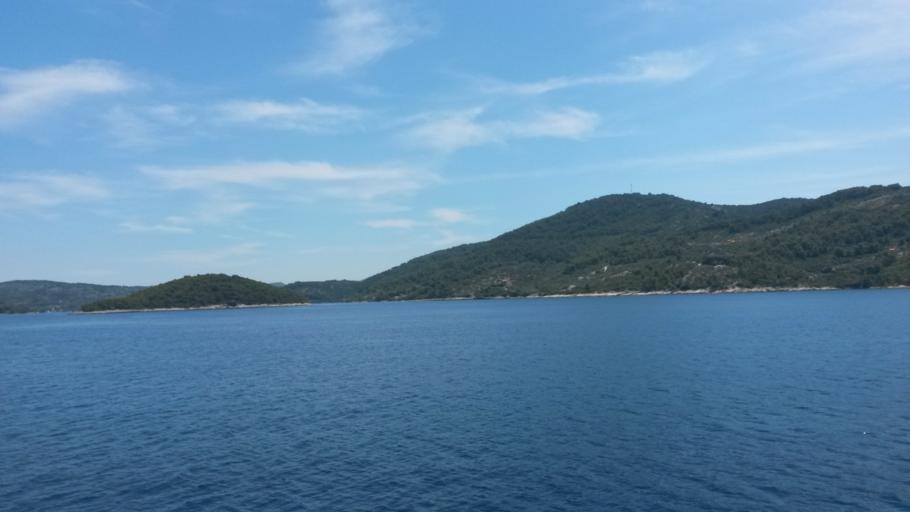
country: HR
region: Dubrovacko-Neretvanska
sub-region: Grad Dubrovnik
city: Vela Luka
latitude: 42.9599
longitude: 16.6614
